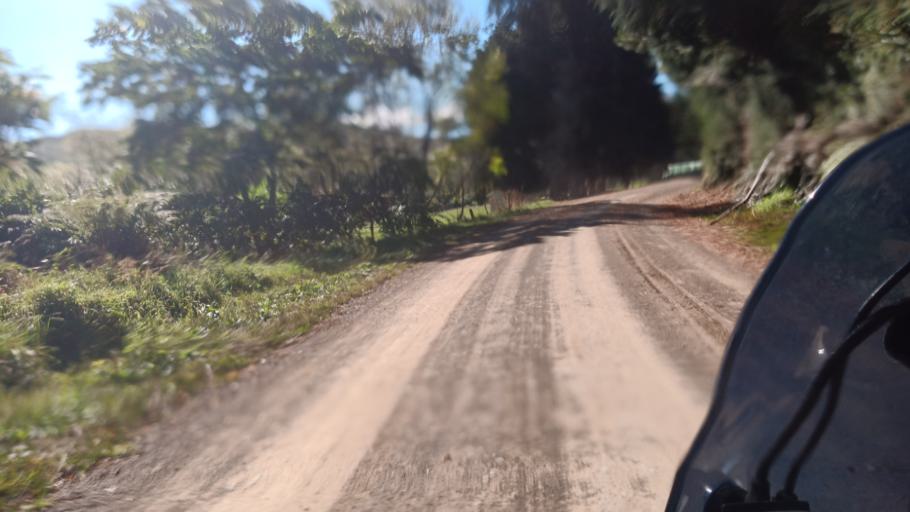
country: NZ
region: Bay of Plenty
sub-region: Opotiki District
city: Opotiki
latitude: -38.2570
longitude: 177.5693
